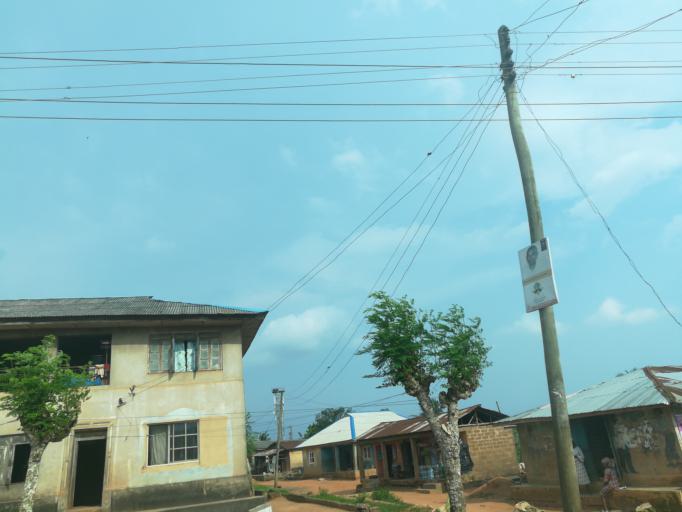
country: NG
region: Lagos
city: Ikorodu
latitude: 6.6632
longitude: 3.6732
